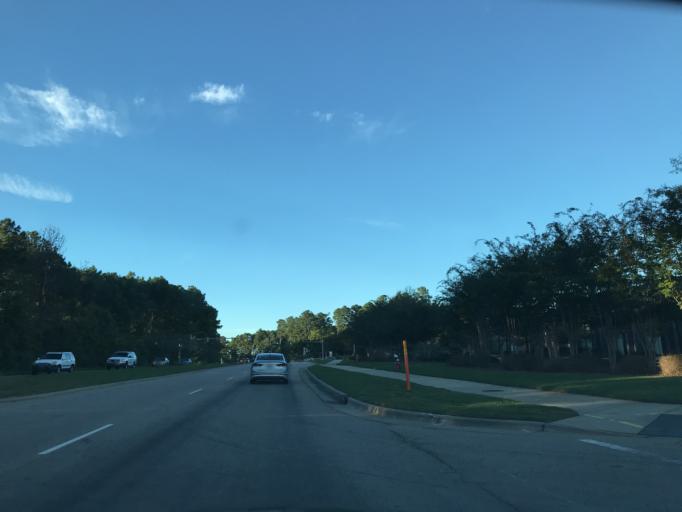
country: US
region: North Carolina
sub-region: Wake County
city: Morrisville
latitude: 35.8551
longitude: -78.8425
